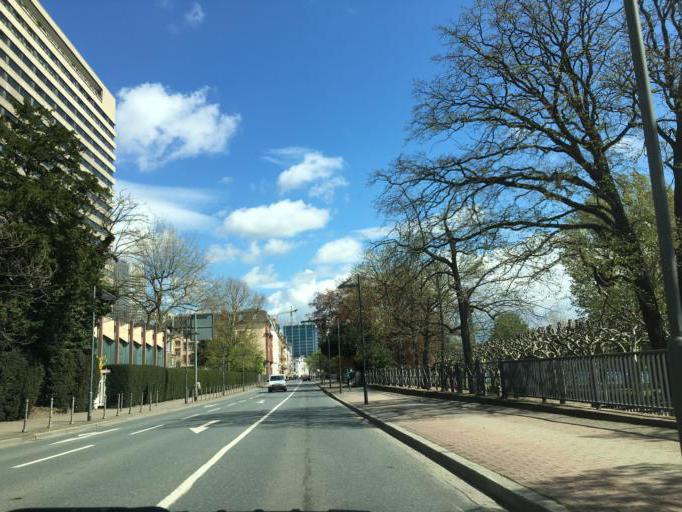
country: DE
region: Hesse
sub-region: Regierungsbezirk Darmstadt
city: Frankfurt am Main
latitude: 50.1037
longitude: 8.6687
